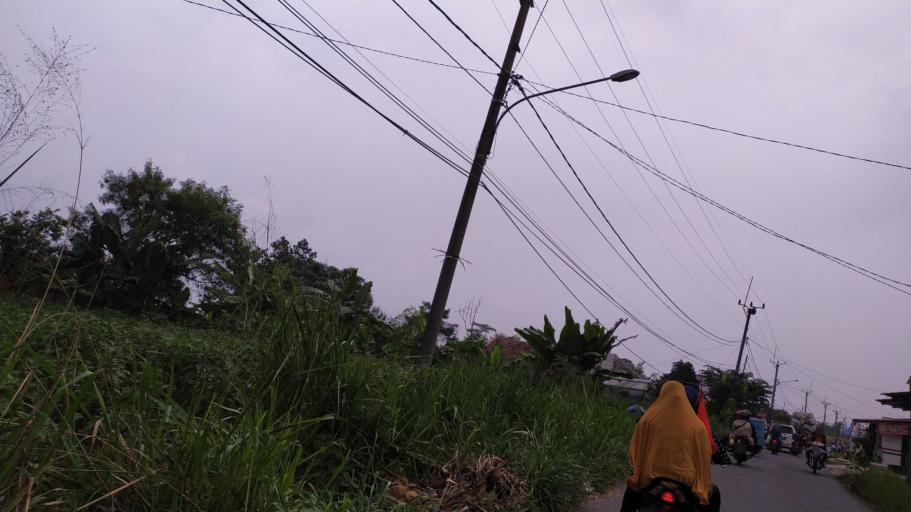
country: ID
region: West Java
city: Ciampea
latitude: -6.6023
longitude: 106.7024
